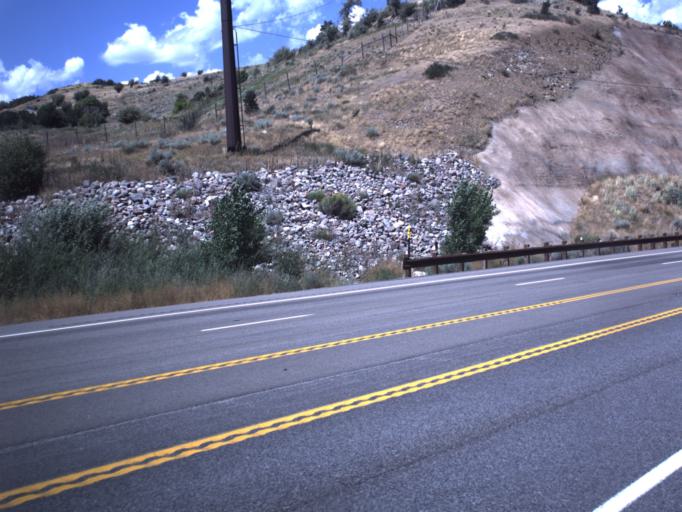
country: US
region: Utah
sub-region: Wasatch County
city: Midway
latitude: 40.3961
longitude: -111.5404
